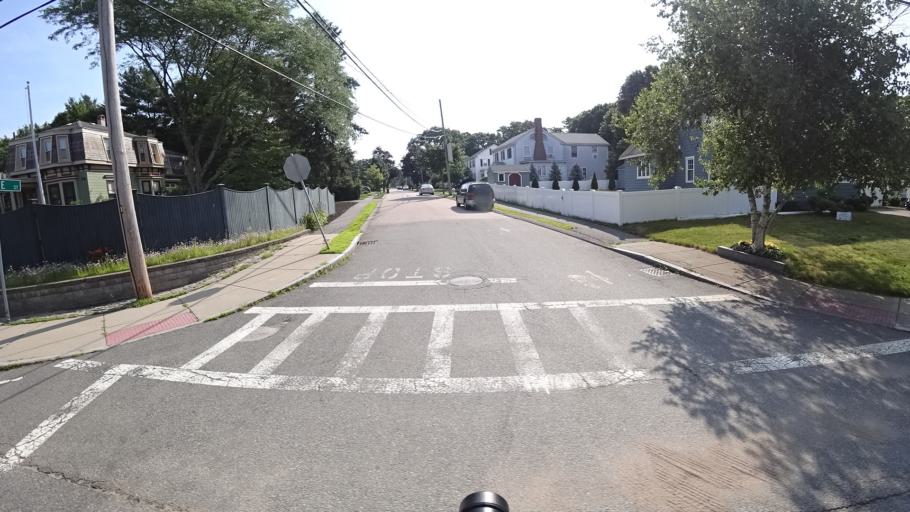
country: US
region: Massachusetts
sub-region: Norfolk County
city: Dedham
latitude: 42.2360
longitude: -71.1630
